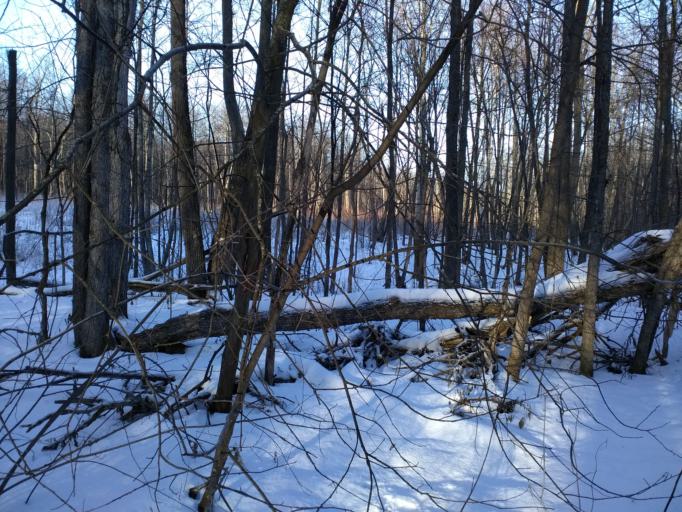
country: RU
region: Bashkortostan
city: Iglino
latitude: 54.8050
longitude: 56.5864
